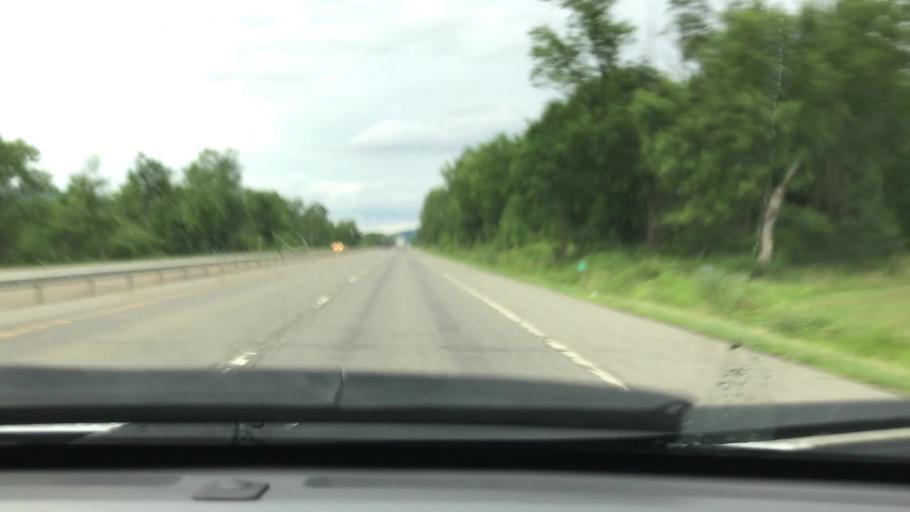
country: US
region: Pennsylvania
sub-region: McKean County
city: Foster Brook
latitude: 42.0390
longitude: -78.6329
